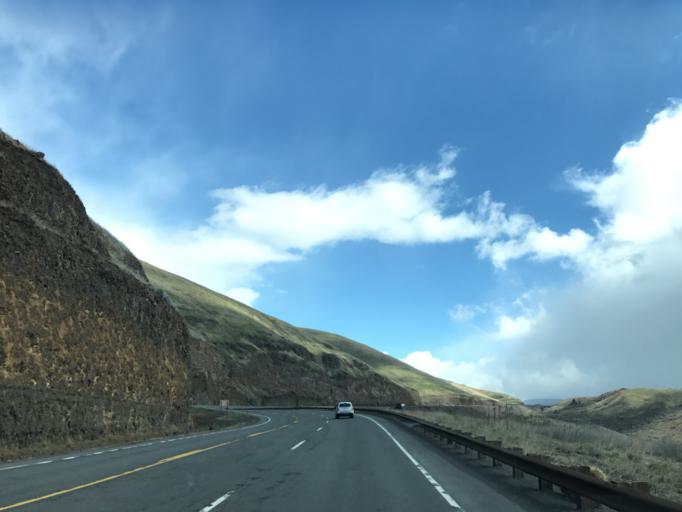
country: US
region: Idaho
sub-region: Idaho County
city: Grangeville
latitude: 45.8158
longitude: -116.2759
